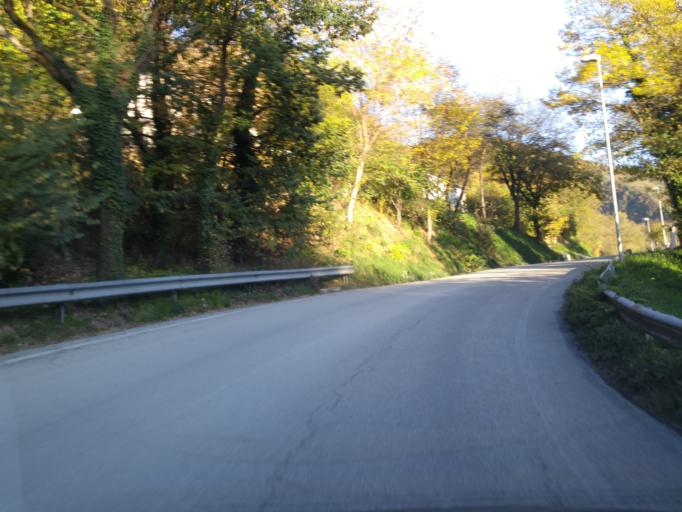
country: IT
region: The Marches
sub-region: Provincia di Pesaro e Urbino
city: Acqualagna
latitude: 43.6388
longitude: 12.7032
